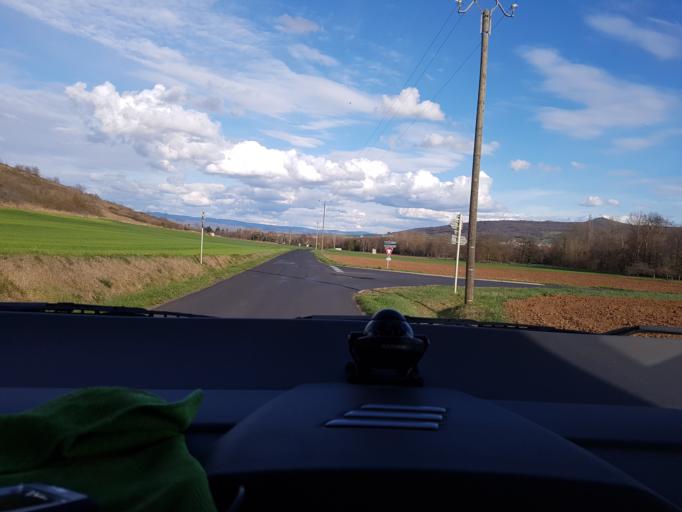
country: FR
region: Auvergne
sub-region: Departement du Puy-de-Dome
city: Saint-Germain-Lembron
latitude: 45.4539
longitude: 3.1938
